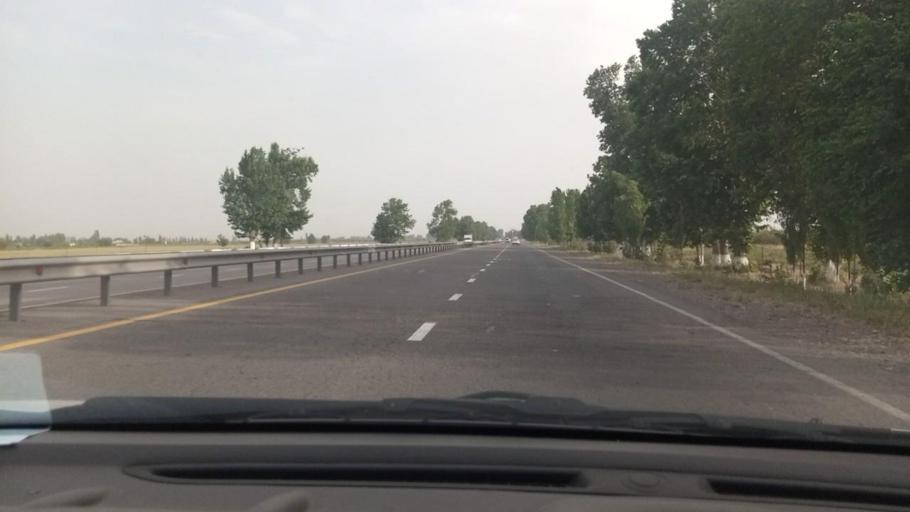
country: UZ
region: Toshkent Shahri
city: Bektemir
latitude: 41.1999
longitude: 69.4029
